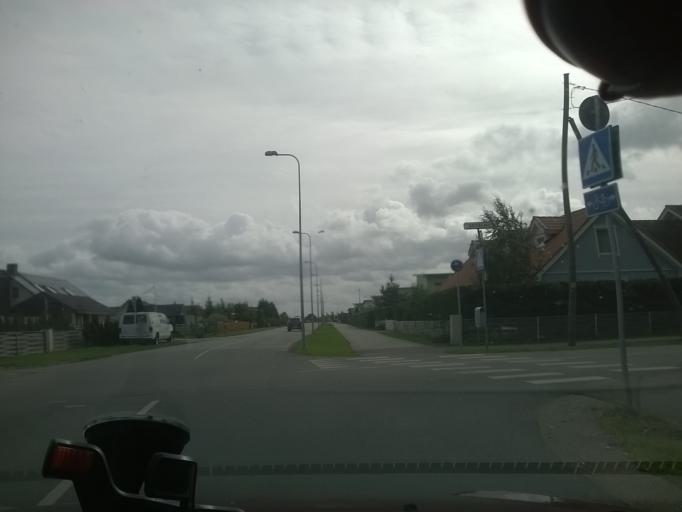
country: EE
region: Harju
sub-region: Tallinna linn
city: Tallinn
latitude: 59.3948
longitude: 24.8143
